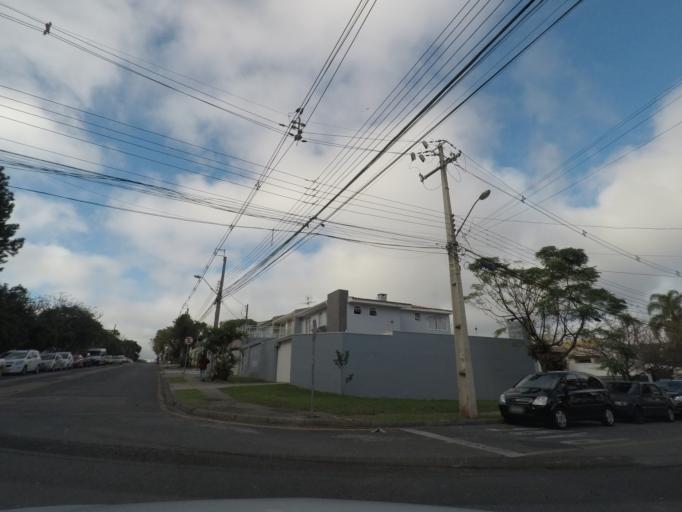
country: BR
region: Parana
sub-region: Curitiba
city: Curitiba
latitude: -25.4538
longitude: -49.2398
